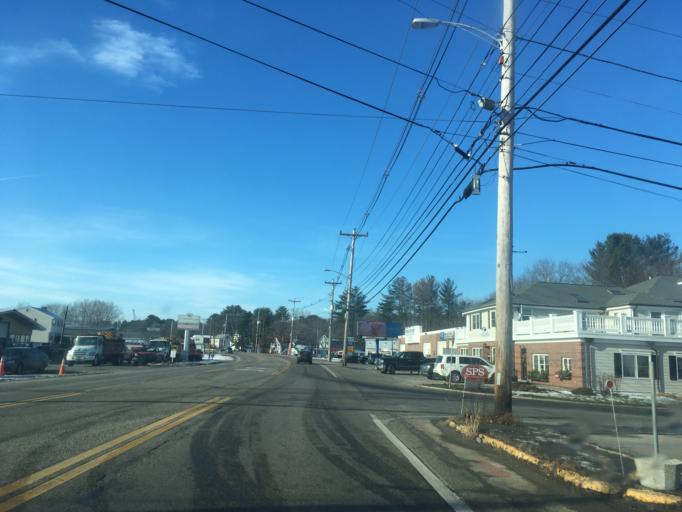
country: US
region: Massachusetts
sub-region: Essex County
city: Salisbury
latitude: 42.8436
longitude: -70.8767
